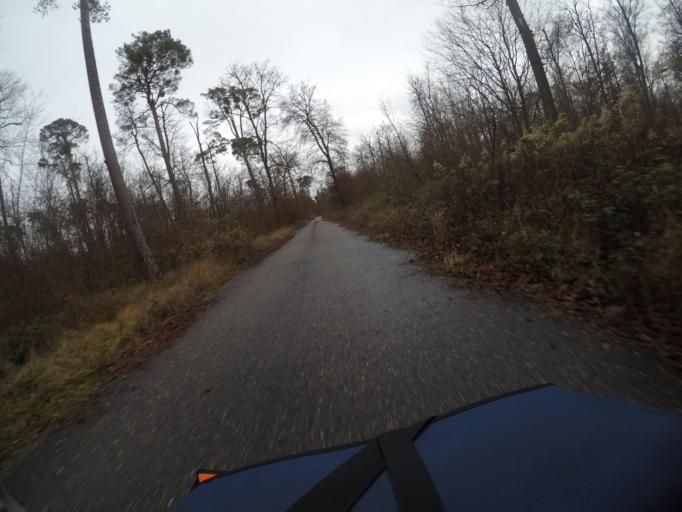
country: DE
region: Baden-Wuerttemberg
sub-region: Karlsruhe Region
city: Philippsburg
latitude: 49.2191
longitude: 8.4791
